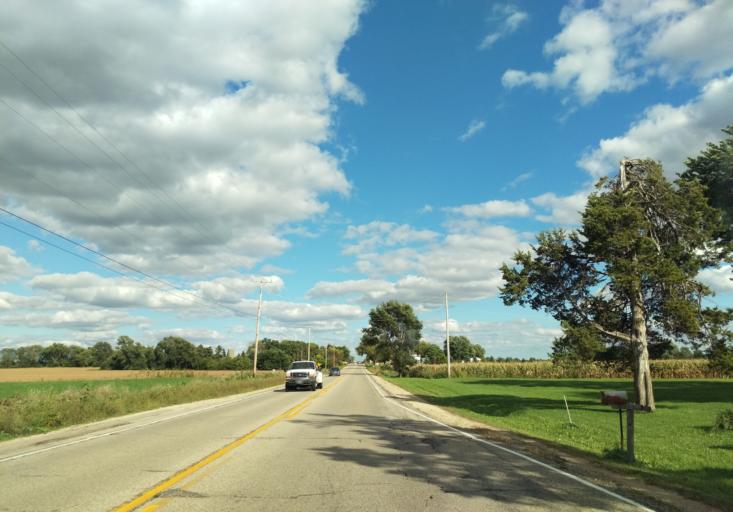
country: US
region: Wisconsin
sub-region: Rock County
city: Janesville
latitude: 42.7304
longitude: -89.0919
